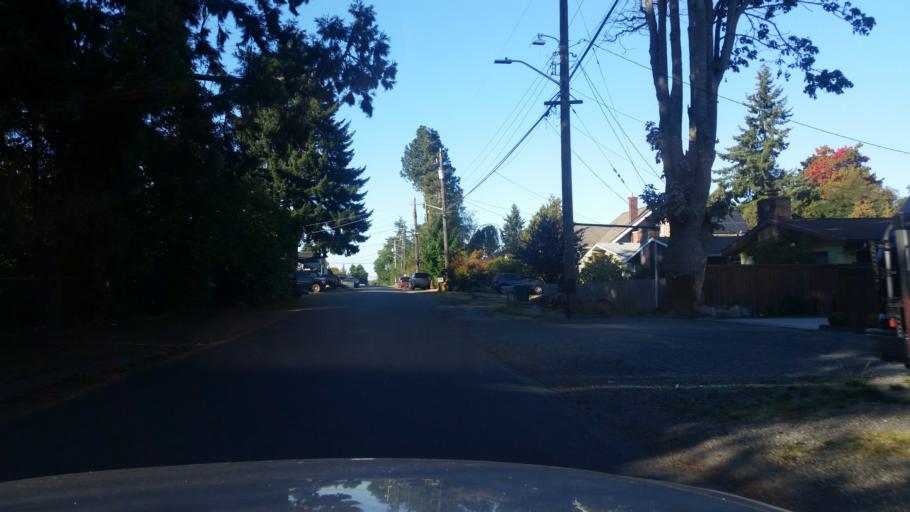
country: US
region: Washington
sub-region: King County
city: Shoreline
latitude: 47.6945
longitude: -122.3715
